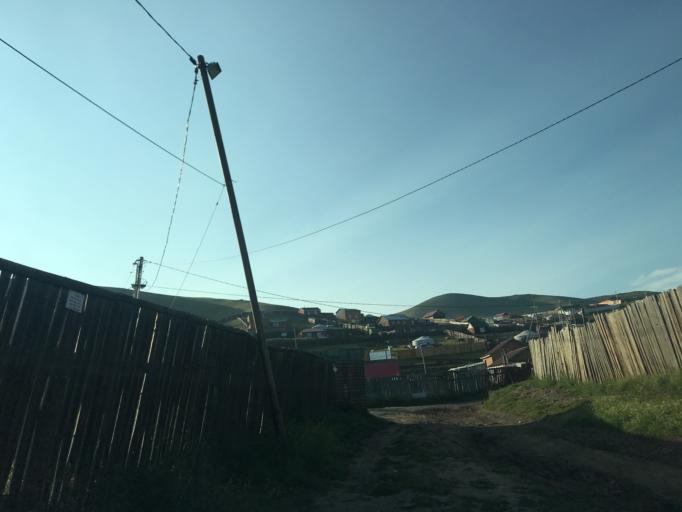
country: MN
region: Ulaanbaatar
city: Ulaanbaatar
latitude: 47.9887
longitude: 106.9618
